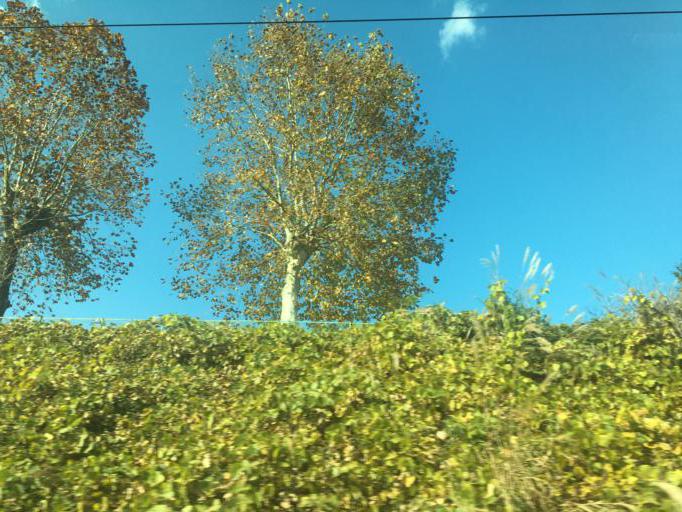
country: JP
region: Ibaraki
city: Tomobe
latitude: 36.3478
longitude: 140.2993
